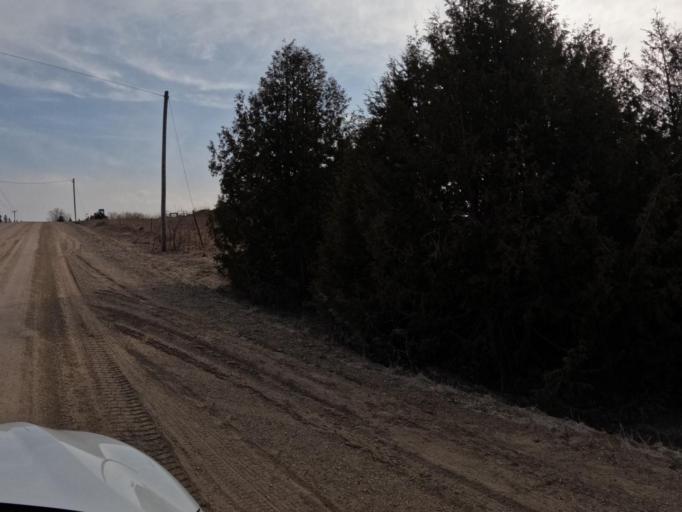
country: CA
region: Ontario
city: Orangeville
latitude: 43.8891
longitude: -80.2988
